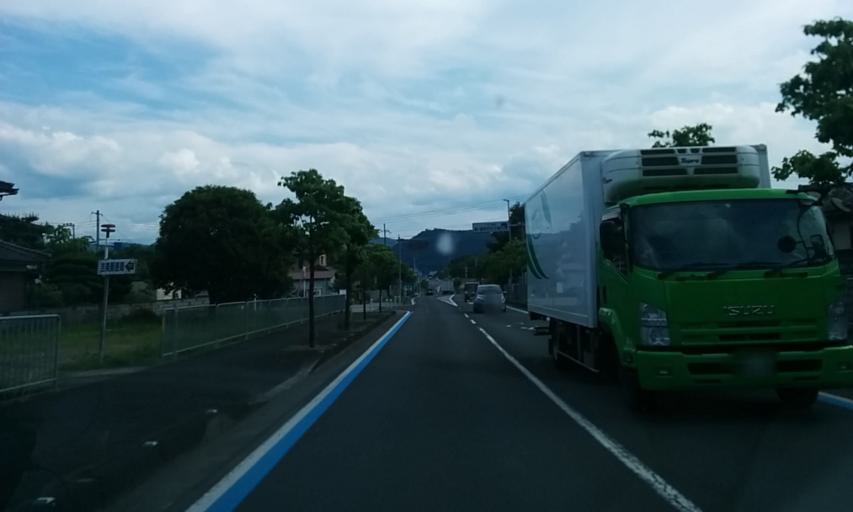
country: JP
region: Kyoto
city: Ayabe
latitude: 35.3150
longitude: 135.2601
